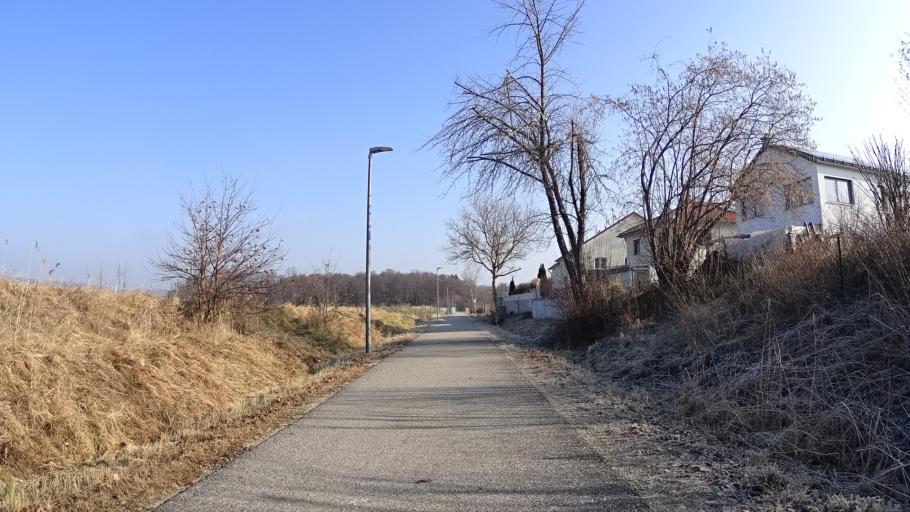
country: DE
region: Bavaria
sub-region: Upper Bavaria
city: Hepberg
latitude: 48.8143
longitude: 11.4947
